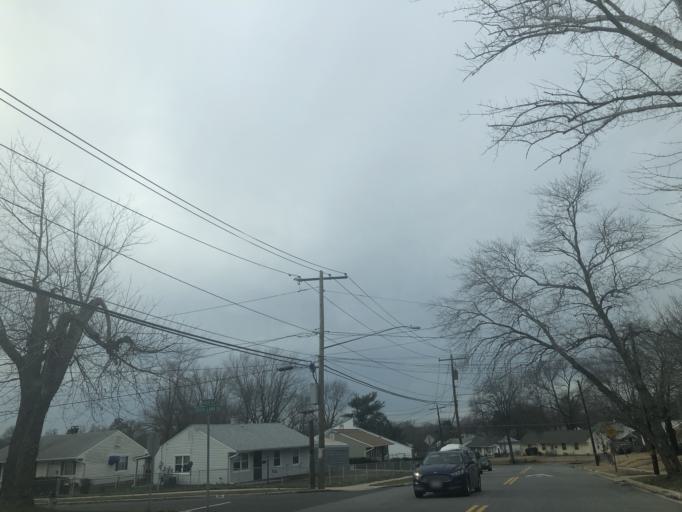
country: US
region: Maryland
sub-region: Prince George's County
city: Oxon Hill
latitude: 38.7927
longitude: -76.9872
